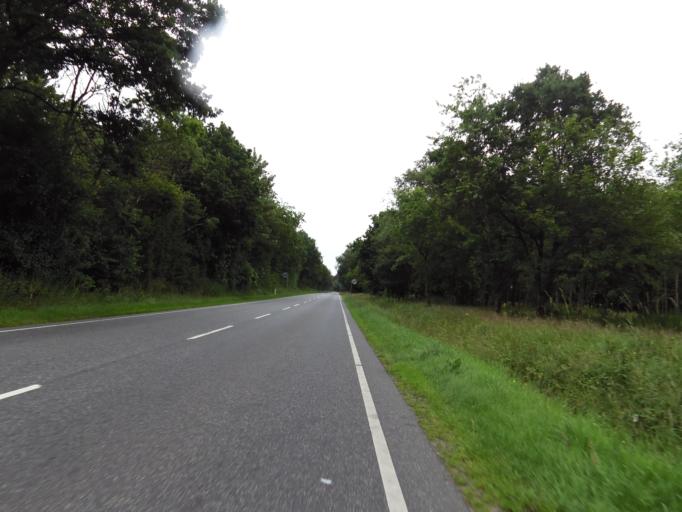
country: DK
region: South Denmark
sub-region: Tonder Kommune
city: Logumkloster
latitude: 55.1560
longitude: 8.9613
